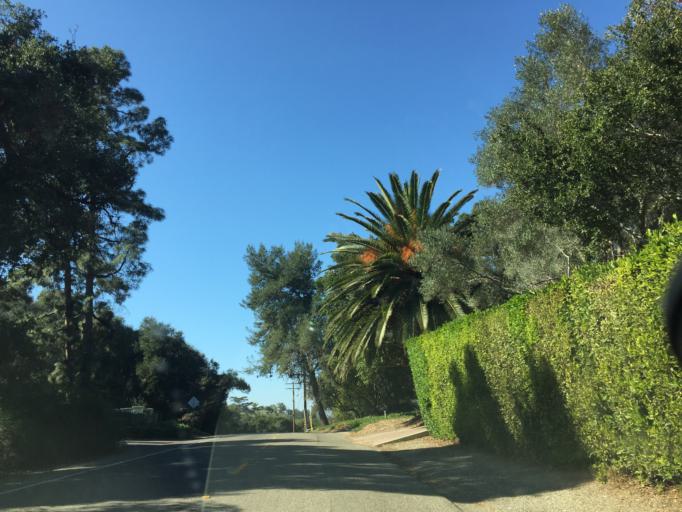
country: US
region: California
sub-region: Santa Barbara County
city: Mission Canyon
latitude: 34.4325
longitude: -119.7652
